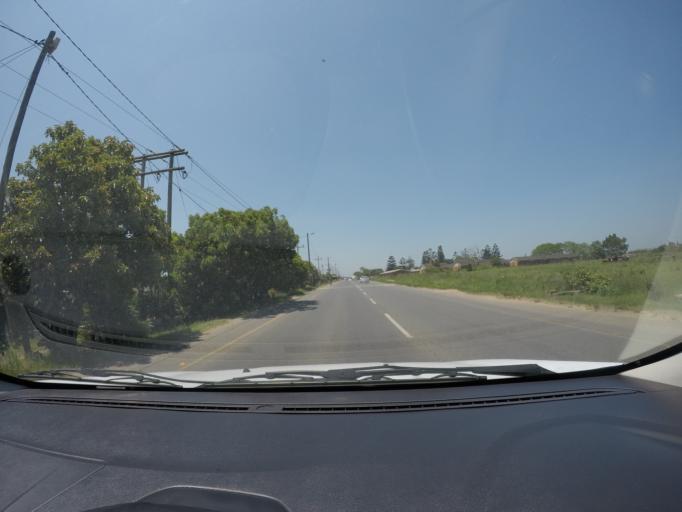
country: ZA
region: KwaZulu-Natal
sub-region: uThungulu District Municipality
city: eSikhawini
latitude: -28.8776
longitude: 31.8933
